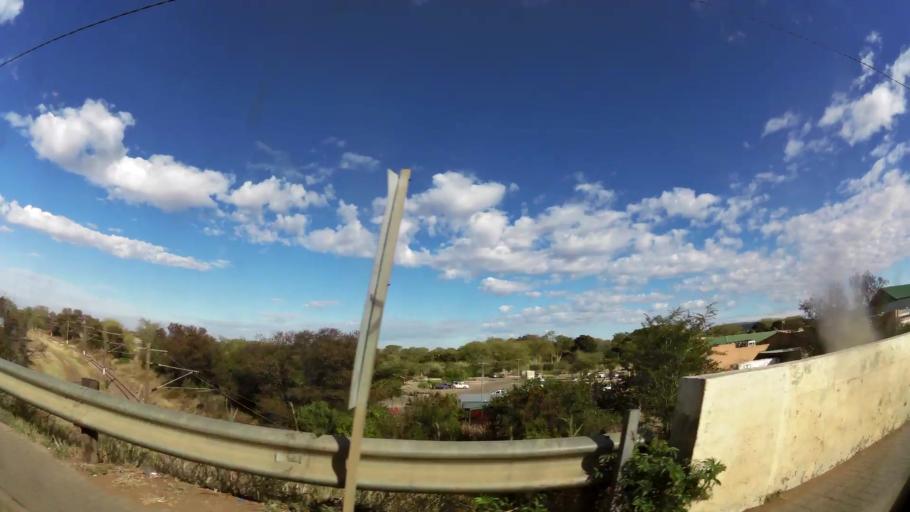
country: ZA
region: Limpopo
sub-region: Waterberg District Municipality
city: Bela-Bela
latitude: -24.8896
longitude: 28.2944
